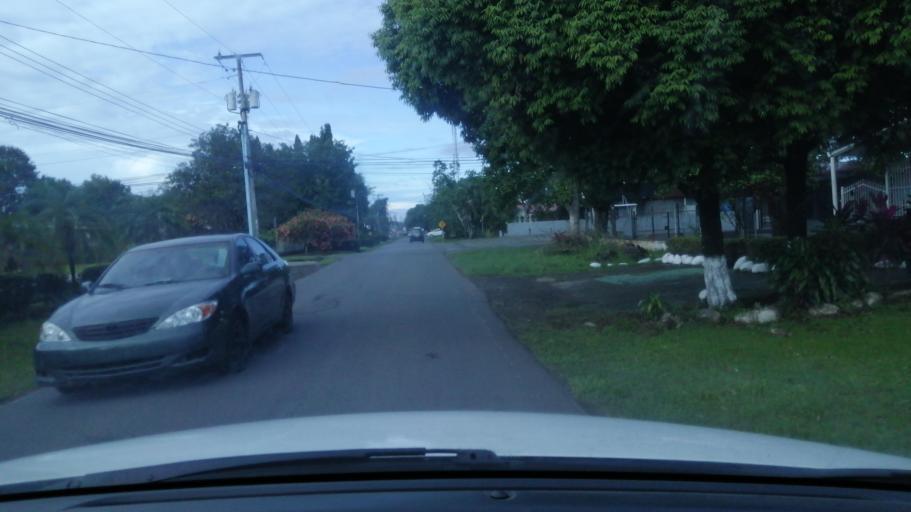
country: PA
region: Chiriqui
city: Mata del Nance
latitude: 8.4499
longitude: -82.4201
